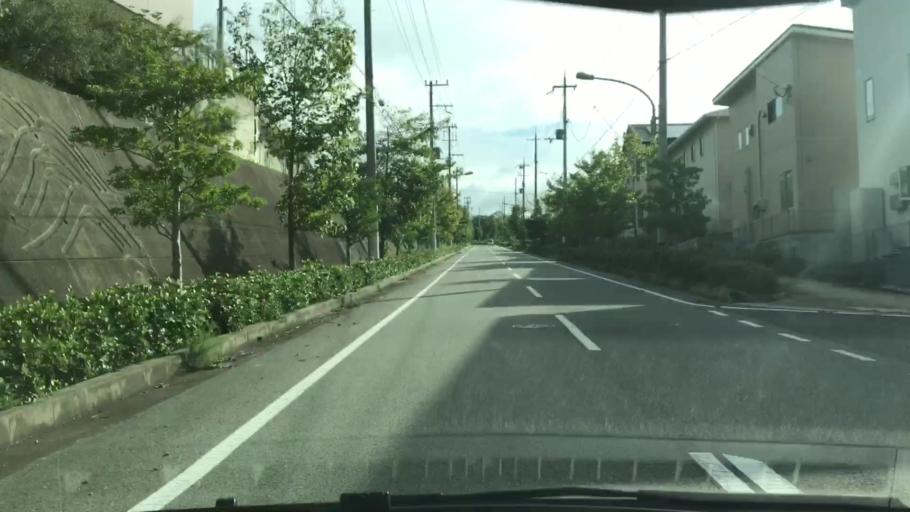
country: JP
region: Hyogo
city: Takarazuka
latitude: 34.8357
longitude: 135.3088
